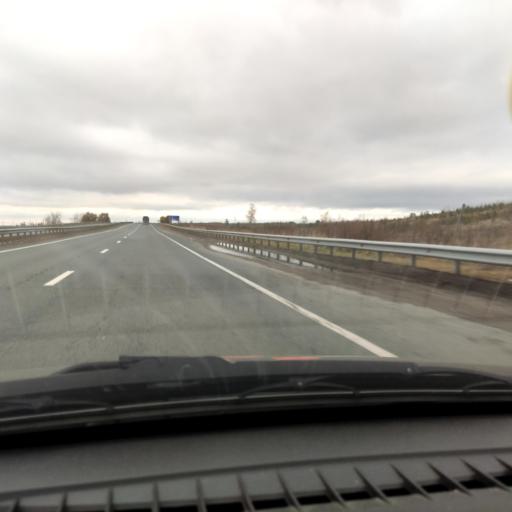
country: RU
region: Samara
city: Zhigulevsk
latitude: 53.5094
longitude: 49.5381
